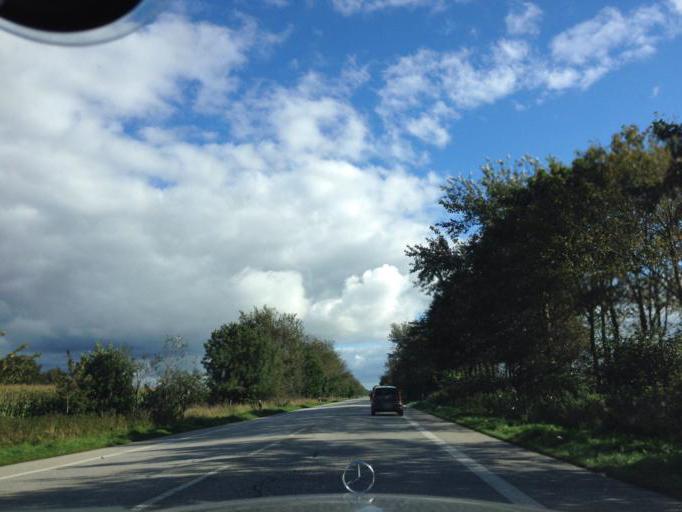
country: DE
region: Schleswig-Holstein
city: Risum-Lindholm
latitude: 54.7591
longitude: 8.8816
